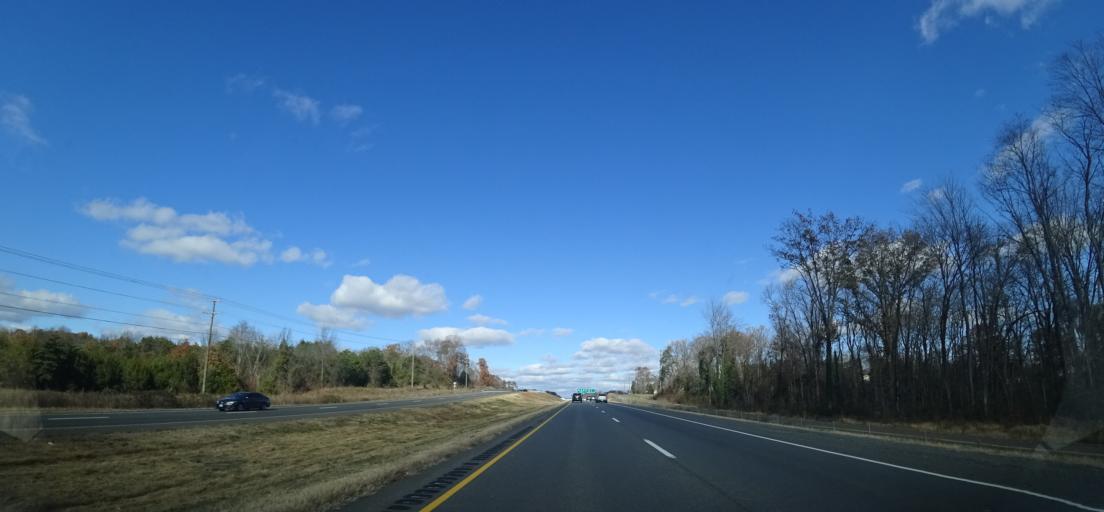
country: US
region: Virginia
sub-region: Fauquier County
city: Bealeton
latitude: 38.6083
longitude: -77.8002
